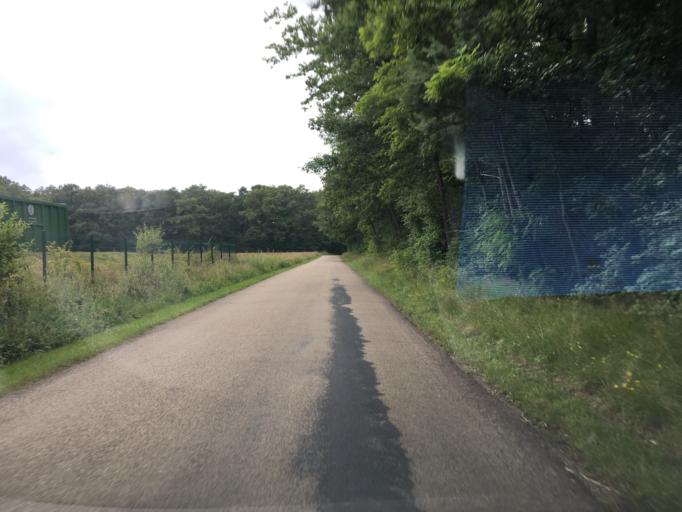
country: FR
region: Bourgogne
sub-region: Departement de l'Yonne
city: Charbuy
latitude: 47.8478
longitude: 3.4934
